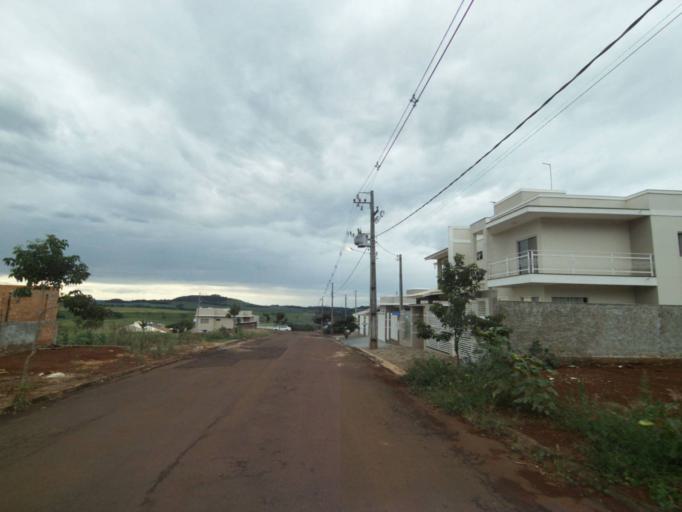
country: BR
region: Parana
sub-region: Guaraniacu
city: Guaraniacu
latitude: -25.0994
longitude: -52.8861
